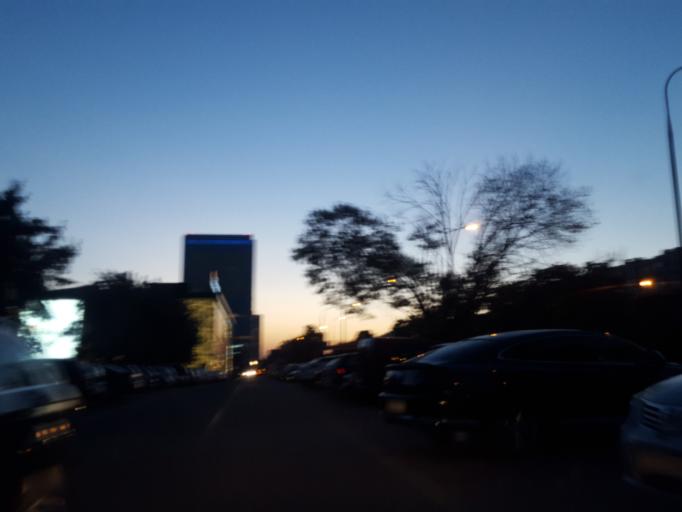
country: PL
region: Masovian Voivodeship
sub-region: Warszawa
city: Praga Poludnie
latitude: 52.2332
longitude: 21.1094
